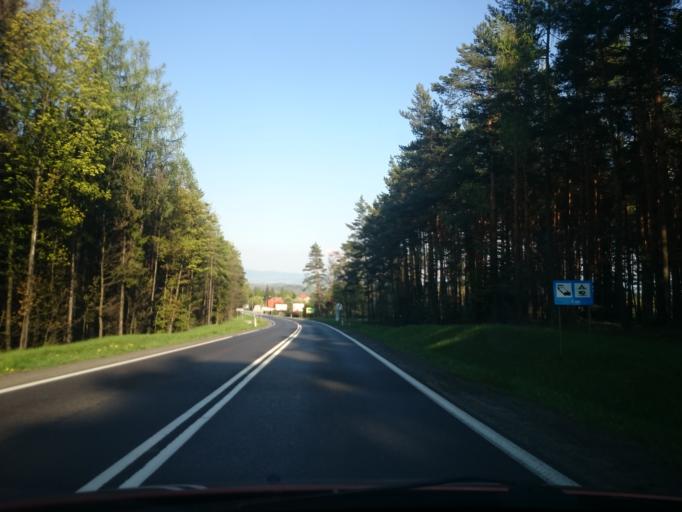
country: PL
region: Lower Silesian Voivodeship
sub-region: Powiat klodzki
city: Polanica-Zdroj
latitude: 50.4225
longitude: 16.4963
